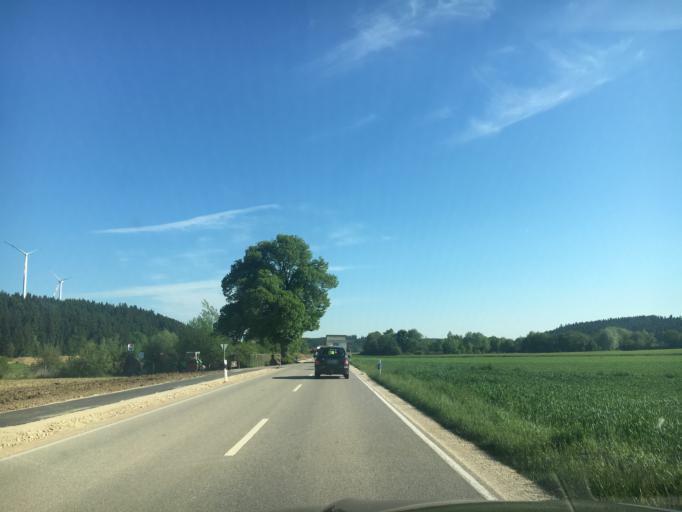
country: DE
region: Bavaria
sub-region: Upper Bavaria
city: Palling
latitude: 48.0099
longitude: 12.6379
